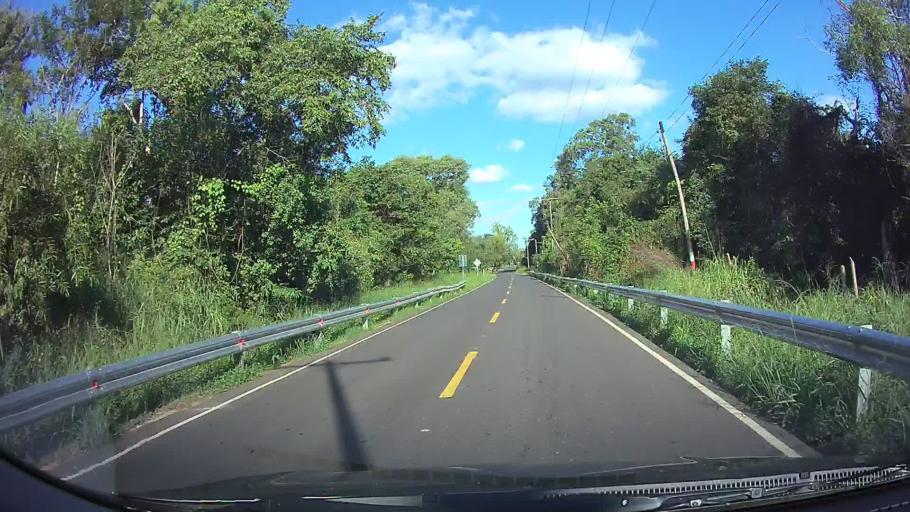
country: PY
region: Central
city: Aregua
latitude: -25.2933
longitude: -57.3932
